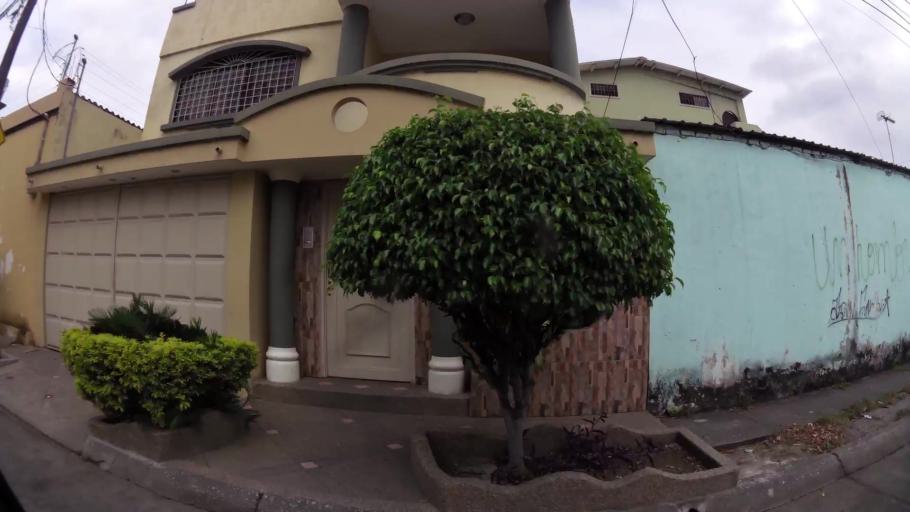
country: EC
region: Guayas
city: Eloy Alfaro
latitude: -2.1198
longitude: -79.8988
